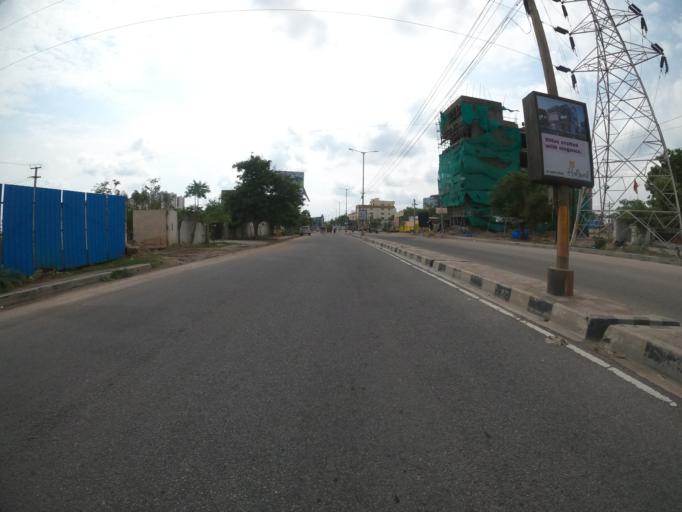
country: IN
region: Telangana
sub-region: Hyderabad
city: Hyderabad
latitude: 17.3828
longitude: 78.3644
